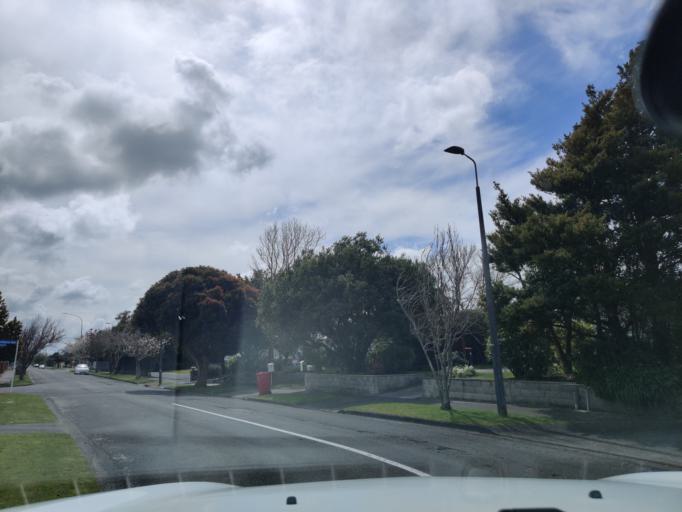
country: NZ
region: Manawatu-Wanganui
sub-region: Palmerston North City
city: Palmerston North
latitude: -40.3789
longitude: 175.5975
